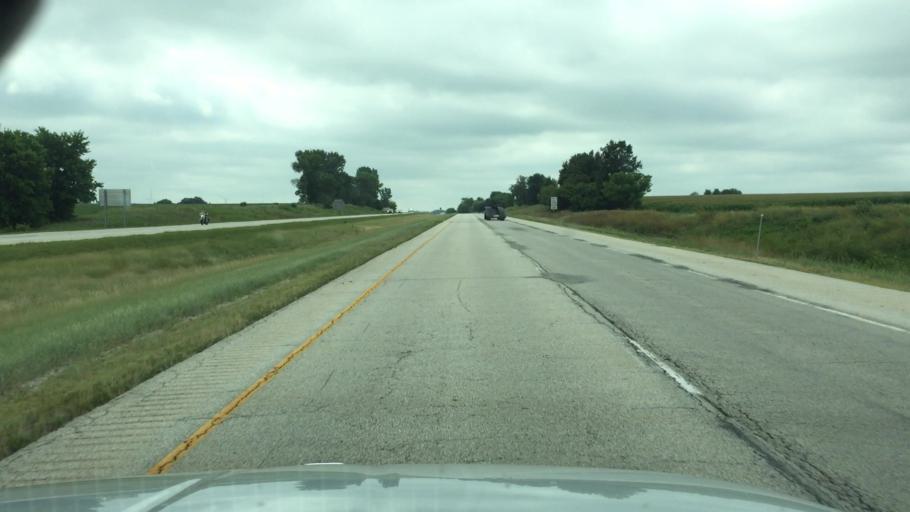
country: US
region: Illinois
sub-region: Henry County
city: Orion
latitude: 41.2875
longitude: -90.3343
